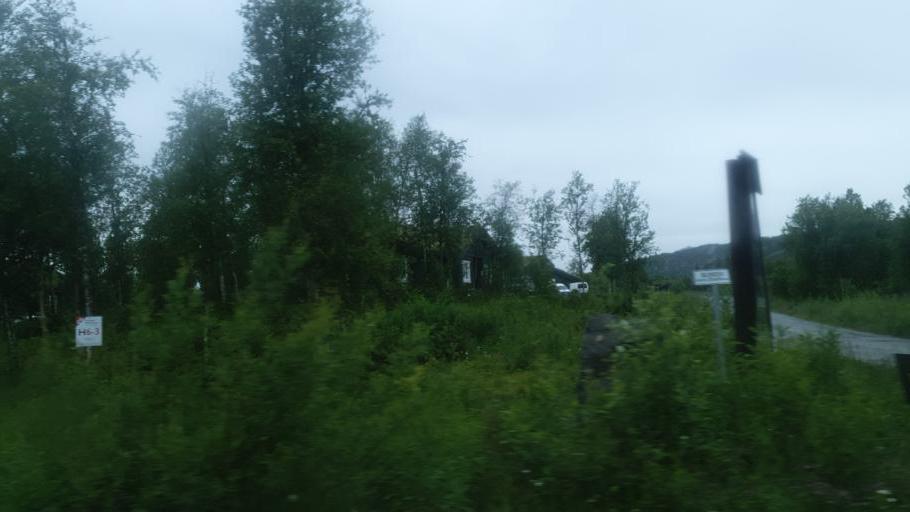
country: NO
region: Oppland
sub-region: Vestre Slidre
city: Slidre
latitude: 61.2397
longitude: 8.9170
